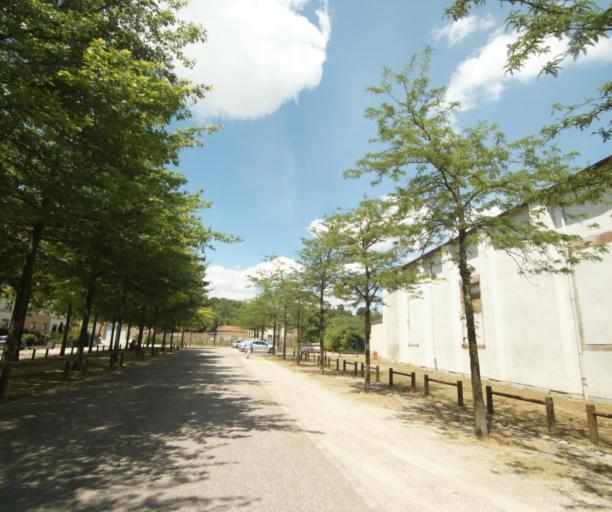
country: FR
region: Lorraine
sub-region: Departement de Meurthe-et-Moselle
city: Luneville
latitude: 48.5989
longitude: 6.4860
